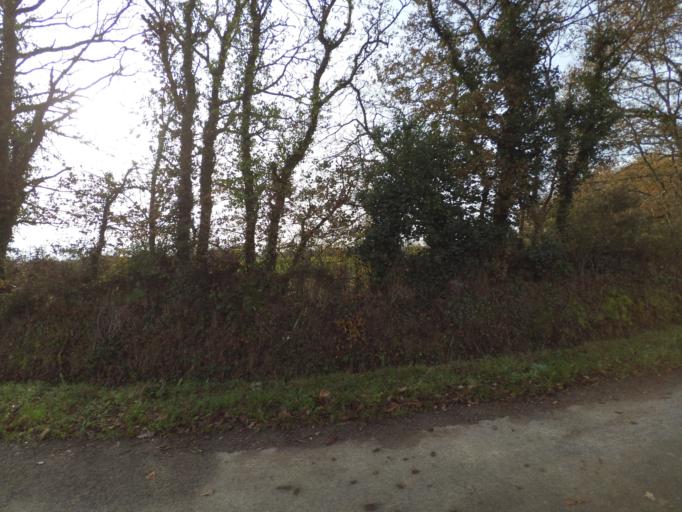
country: FR
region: Pays de la Loire
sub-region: Departement de la Loire-Atlantique
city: La Planche
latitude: 47.0097
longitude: -1.4061
